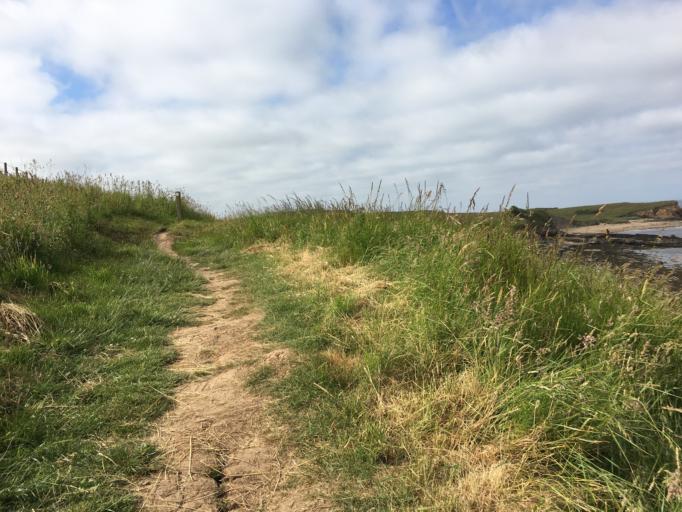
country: GB
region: England
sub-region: Northumberland
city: Alnmouth
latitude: 55.4439
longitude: -1.5900
